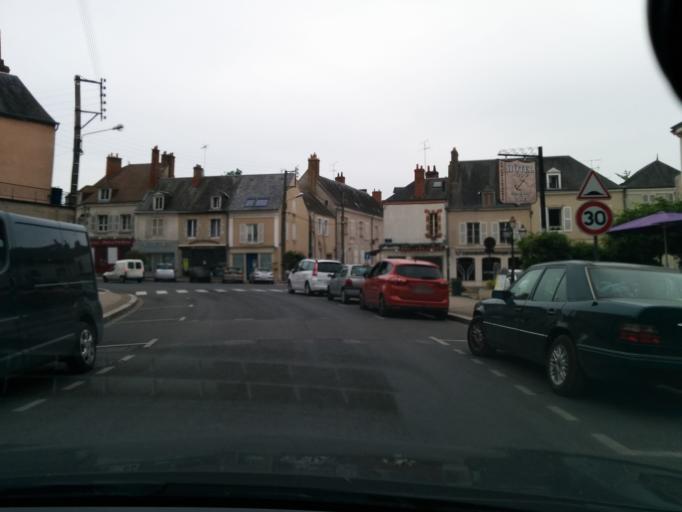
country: FR
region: Centre
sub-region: Departement du Loiret
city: Chateauneuf-sur-Loire
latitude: 47.8645
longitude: 2.2191
